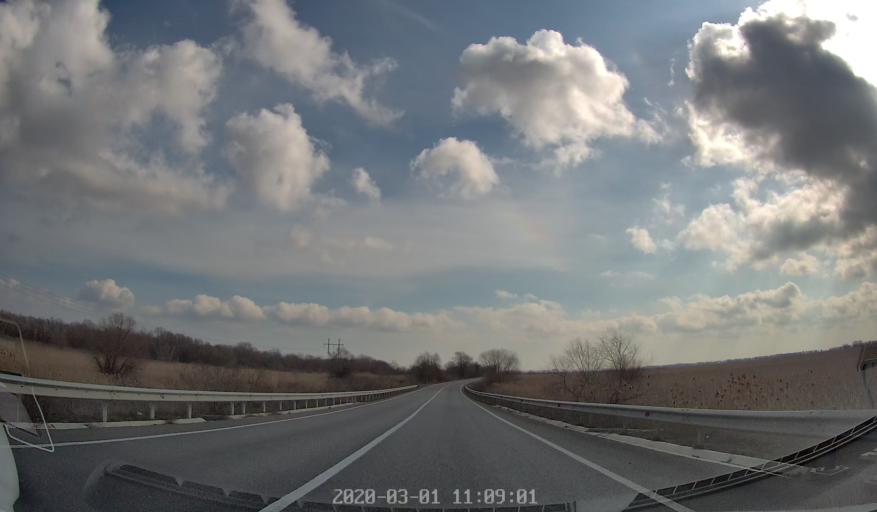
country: UA
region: Odessa
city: Bilyayivka
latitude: 46.4150
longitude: 30.1572
